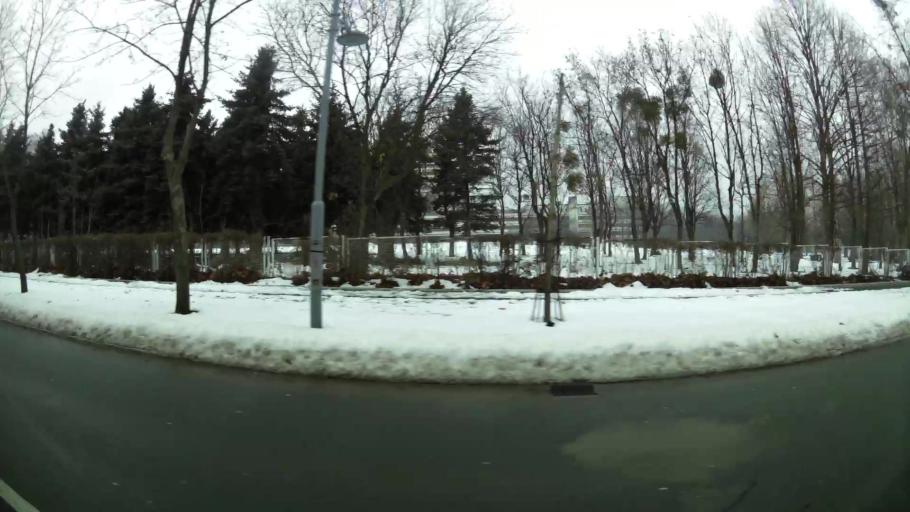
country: RS
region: Central Serbia
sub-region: Belgrade
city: Vozdovac
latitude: 44.7626
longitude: 20.4697
